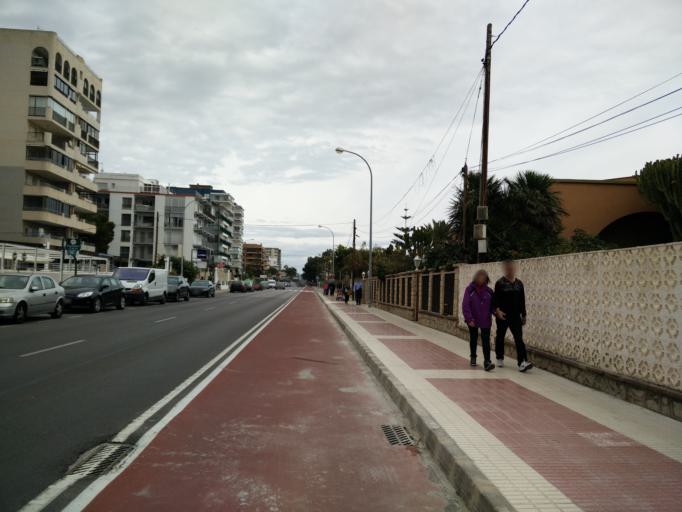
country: ES
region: Valencia
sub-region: Provincia de Castello
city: Benicassim
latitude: 40.0386
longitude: 0.0529
